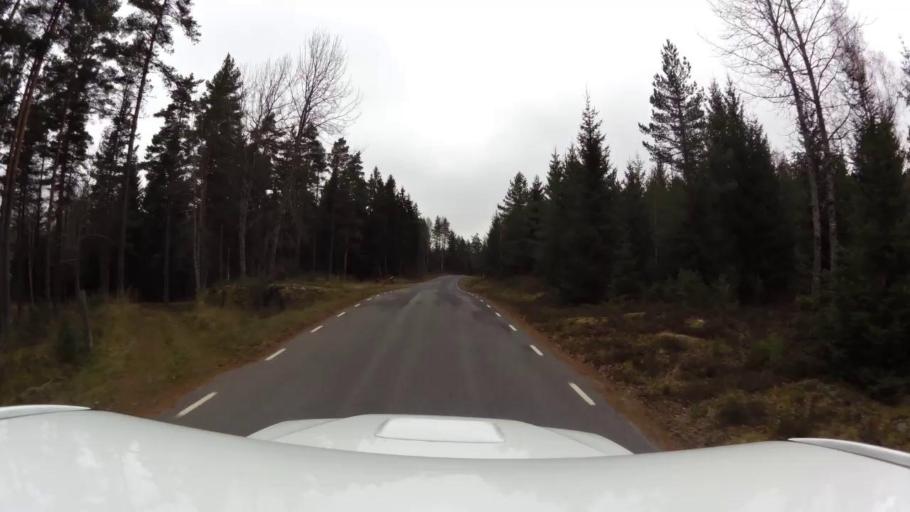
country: SE
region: OEstergoetland
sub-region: Kinda Kommun
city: Rimforsa
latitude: 58.1404
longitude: 15.4538
